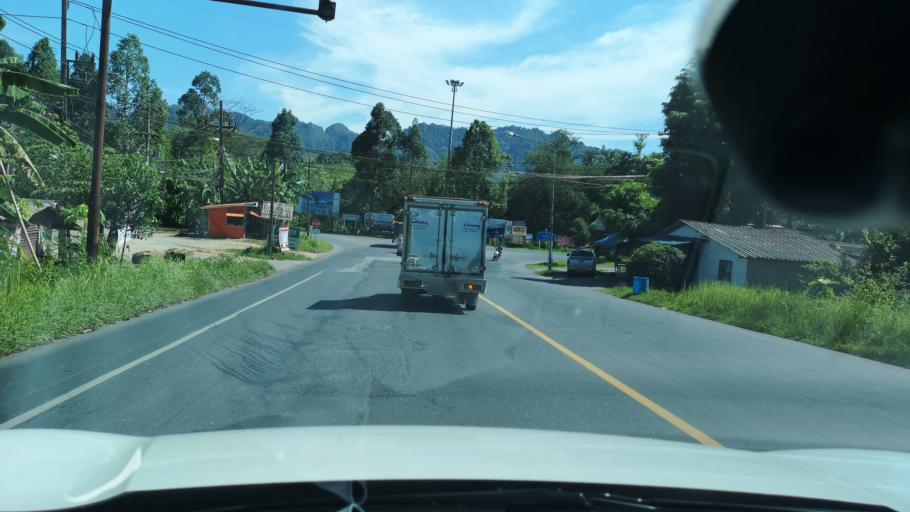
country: TH
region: Phangnga
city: Phang Nga
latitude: 8.5260
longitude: 98.5194
